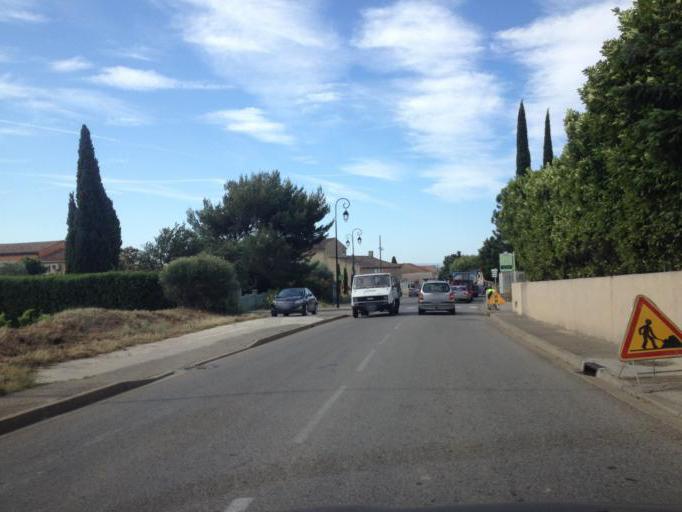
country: FR
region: Provence-Alpes-Cote d'Azur
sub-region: Departement du Vaucluse
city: Chateauneuf-du-Pape
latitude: 44.0560
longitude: 4.8352
